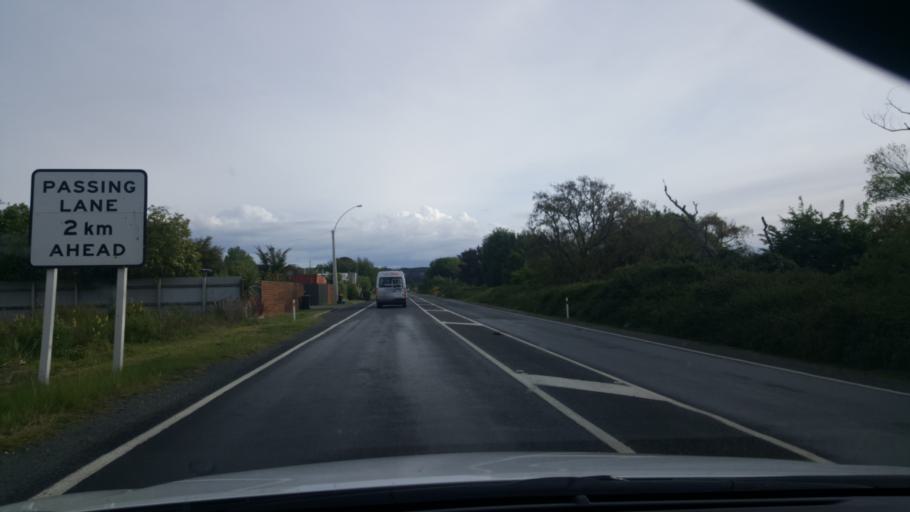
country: NZ
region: Waikato
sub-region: Taupo District
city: Taupo
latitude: -38.7789
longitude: 176.0770
